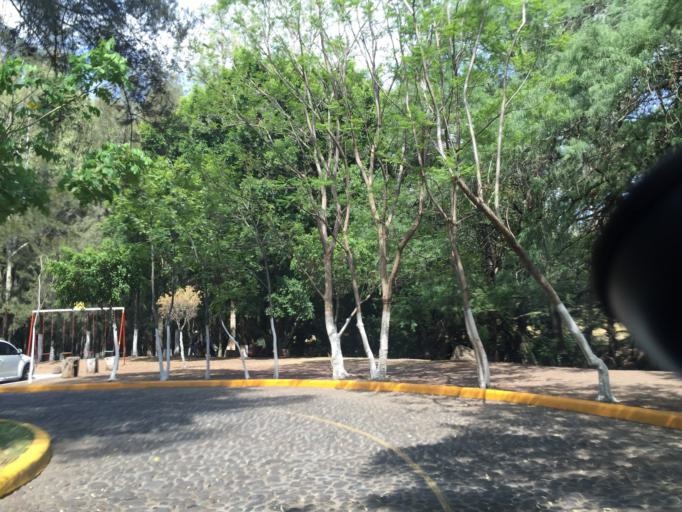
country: MX
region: Jalisco
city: Atotonilco el Alto
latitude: 20.5633
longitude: -102.4762
